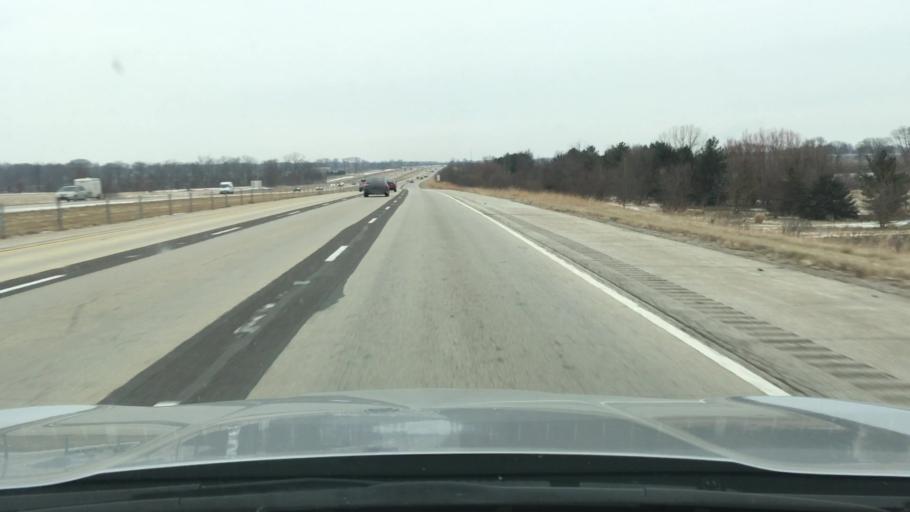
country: US
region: Illinois
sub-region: Sangamon County
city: Divernon
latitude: 39.6326
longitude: -89.6467
